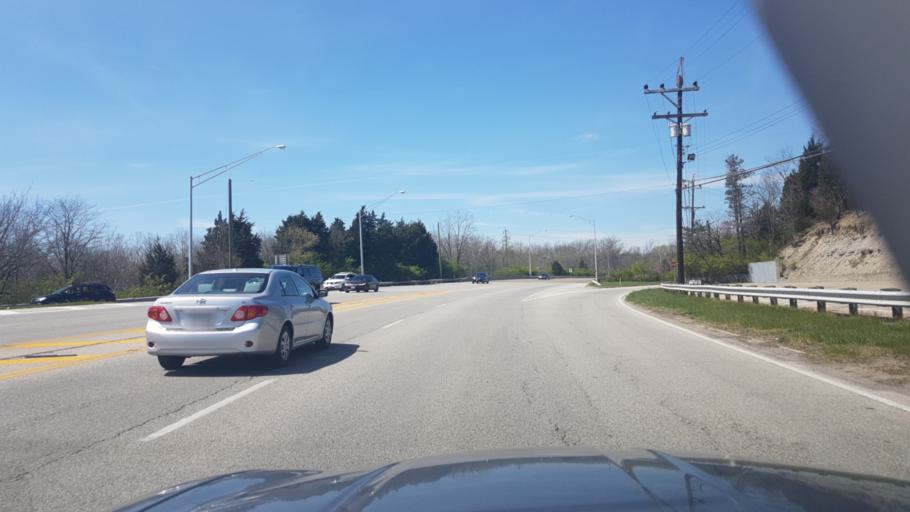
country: US
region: Ohio
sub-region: Hamilton County
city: Turpin Hills
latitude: 39.1069
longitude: -84.3986
